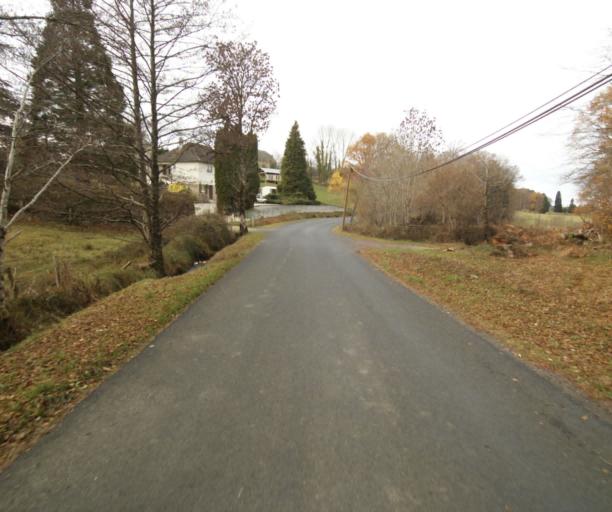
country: FR
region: Limousin
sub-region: Departement de la Correze
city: Beynat
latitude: 45.1736
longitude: 1.7263
